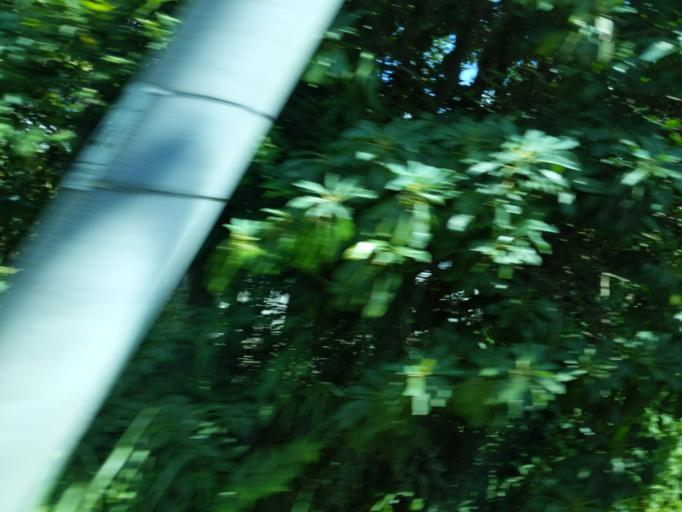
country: JP
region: Tokyo
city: Chofugaoka
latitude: 35.6232
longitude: 139.5624
